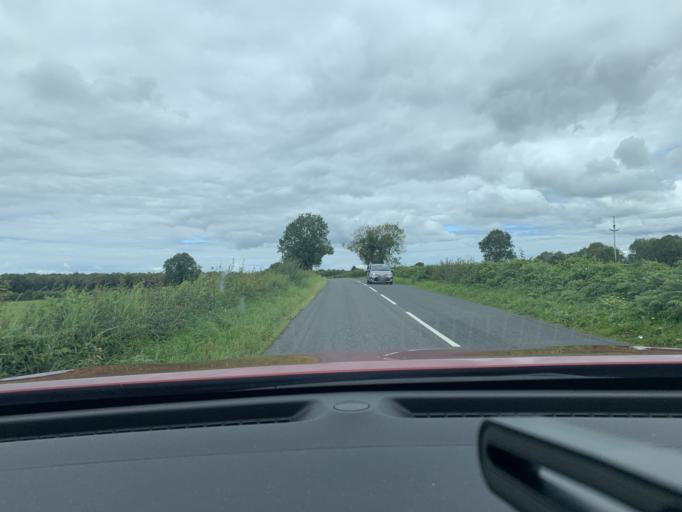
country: GB
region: Northern Ireland
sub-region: Fermanagh District
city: Enniskillen
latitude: 54.2831
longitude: -7.7005
